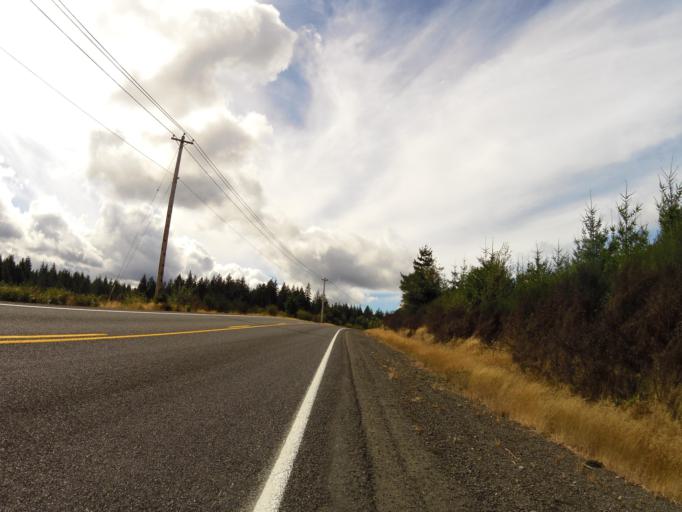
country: US
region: Washington
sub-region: Mason County
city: Shelton
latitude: 47.1482
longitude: -123.0705
